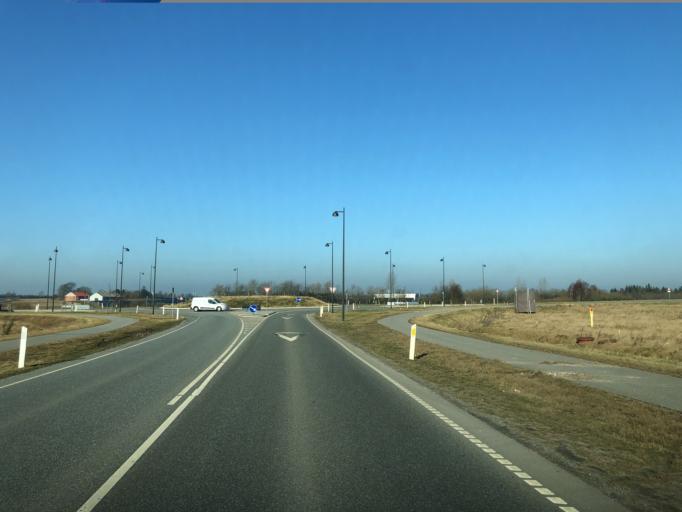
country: DK
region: Central Jutland
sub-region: Silkeborg Kommune
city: Silkeborg
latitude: 56.2033
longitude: 9.5561
